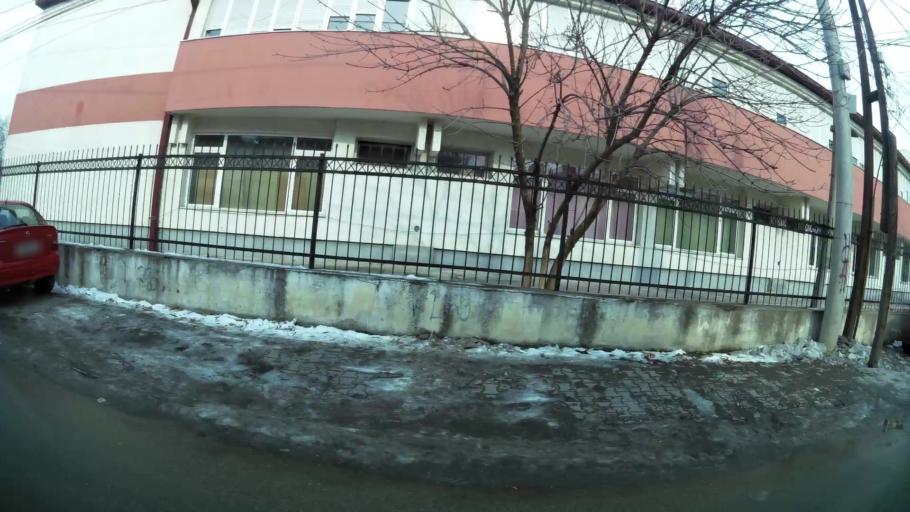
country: MK
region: Cair
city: Cair
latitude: 42.0104
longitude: 21.4396
